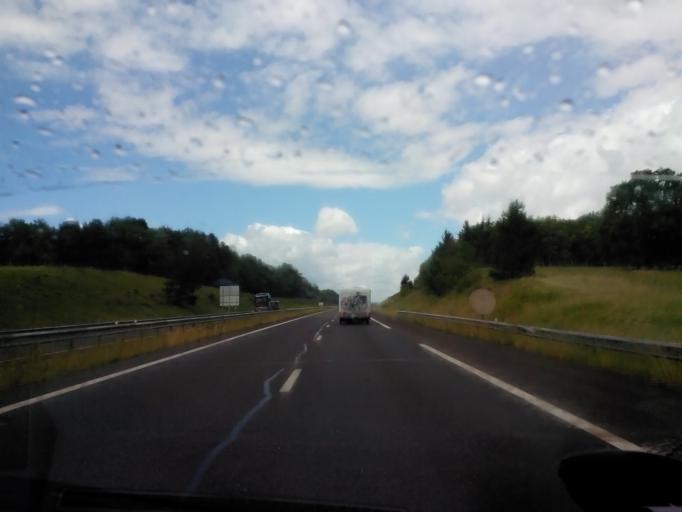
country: FR
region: Lorraine
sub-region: Departement de Meurthe-et-Moselle
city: Dommartin-les-Toul
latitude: 48.6357
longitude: 5.8813
